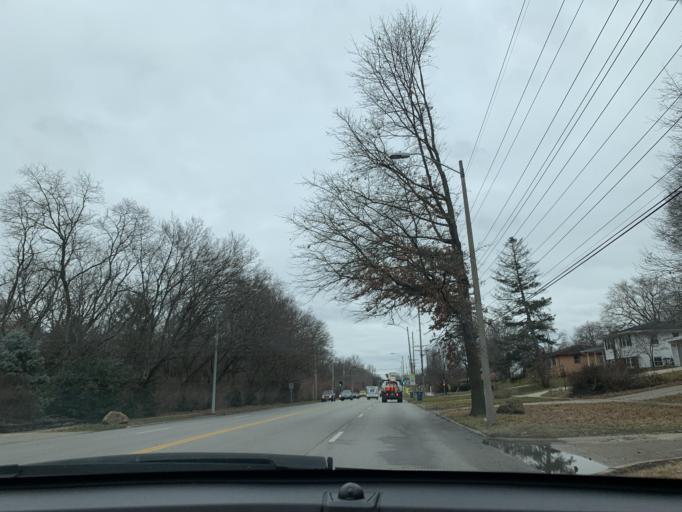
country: US
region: Illinois
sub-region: Sangamon County
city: Leland Grove
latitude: 39.7738
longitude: -89.6868
